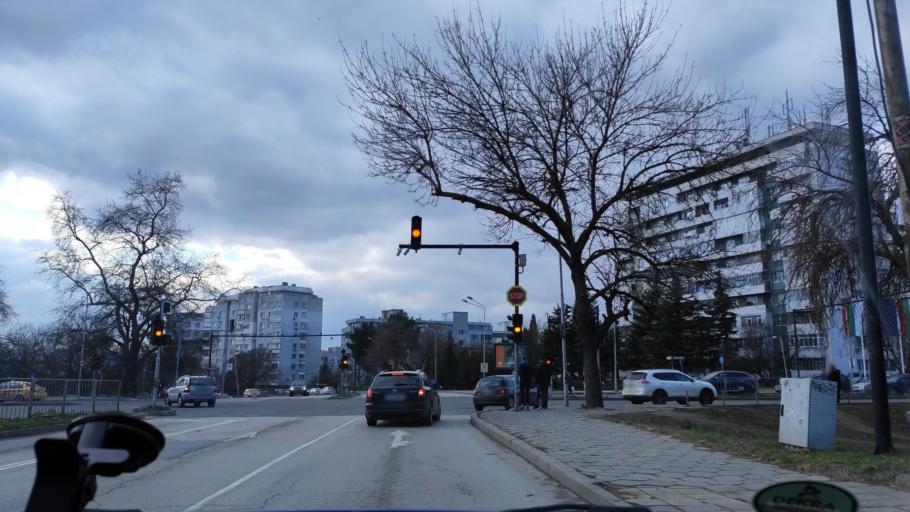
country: BG
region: Varna
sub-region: Obshtina Varna
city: Varna
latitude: 43.2198
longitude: 27.8883
